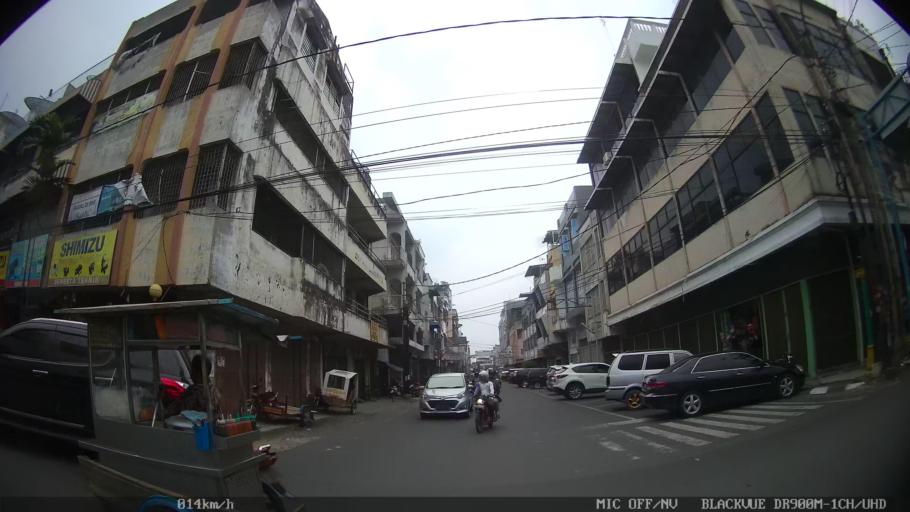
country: ID
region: North Sumatra
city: Medan
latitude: 3.5834
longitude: 98.6874
